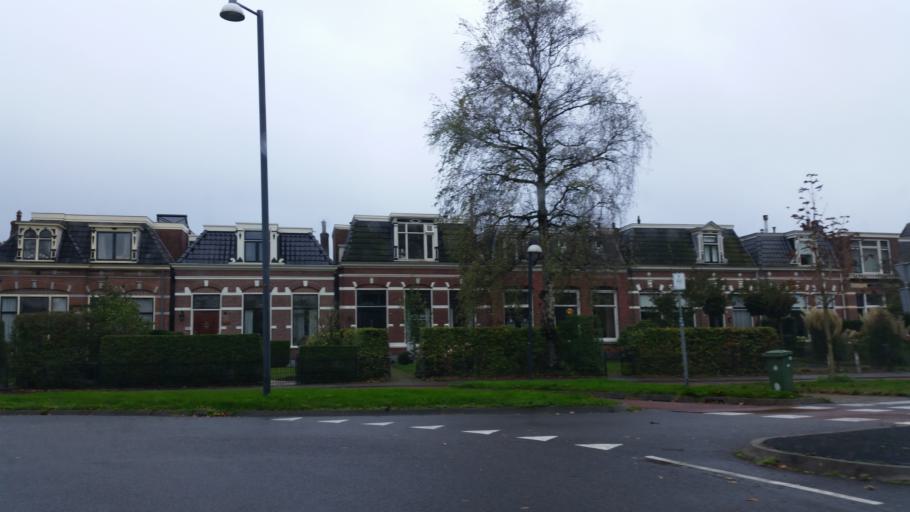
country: NL
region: Friesland
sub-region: Gemeente Leeuwarden
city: Bilgaard
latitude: 53.2071
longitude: 5.7944
